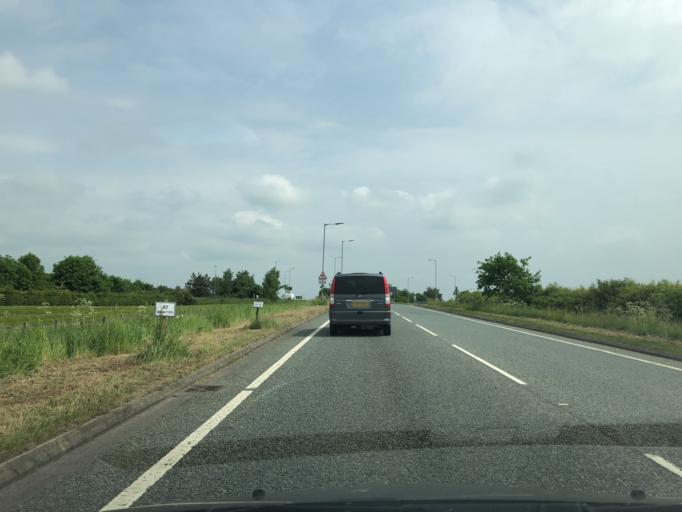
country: GB
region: England
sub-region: North Yorkshire
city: Boroughbridge
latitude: 54.1522
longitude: -1.4296
